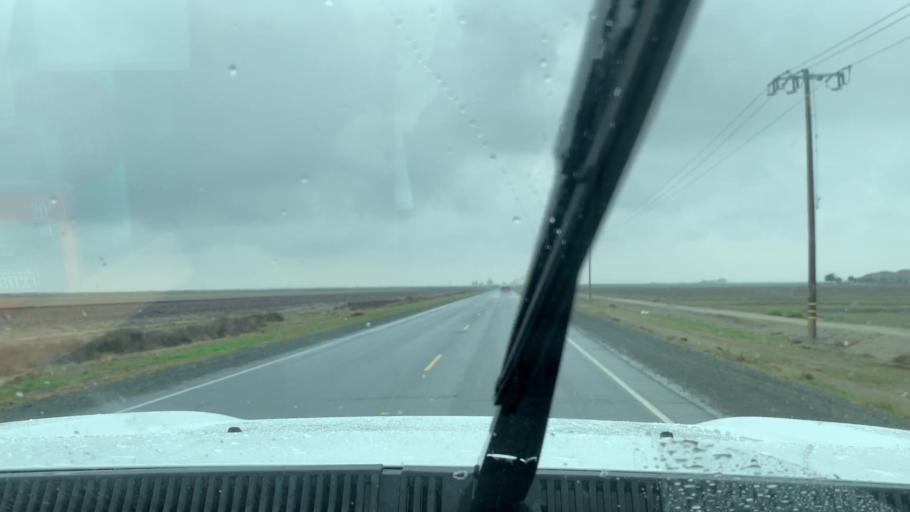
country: US
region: California
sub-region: Tulare County
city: Alpaugh
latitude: 35.9643
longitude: -119.4585
